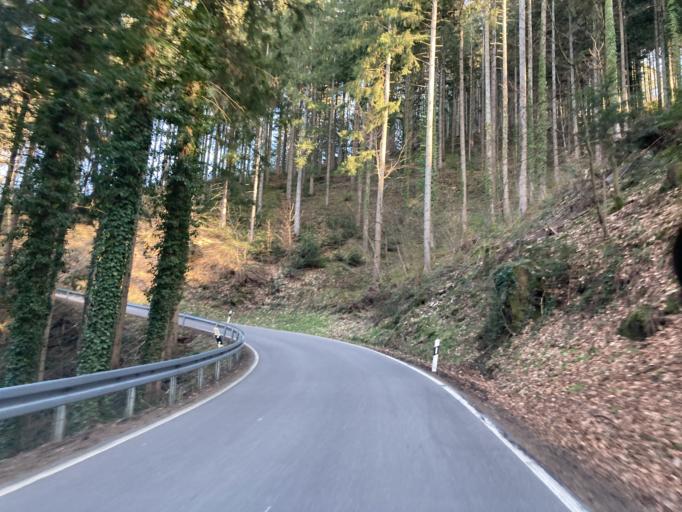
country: DE
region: Baden-Wuerttemberg
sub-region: Freiburg Region
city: Oppenau
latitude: 48.4799
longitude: 8.1884
